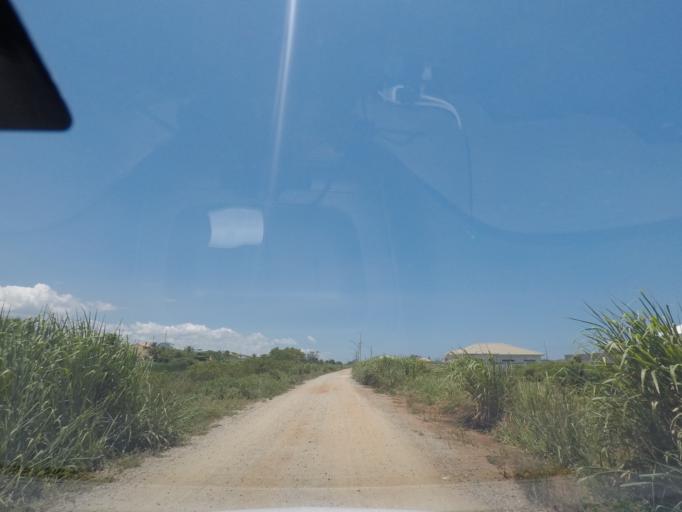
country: BR
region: Rio de Janeiro
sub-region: Niteroi
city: Niteroi
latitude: -22.9680
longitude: -42.9915
